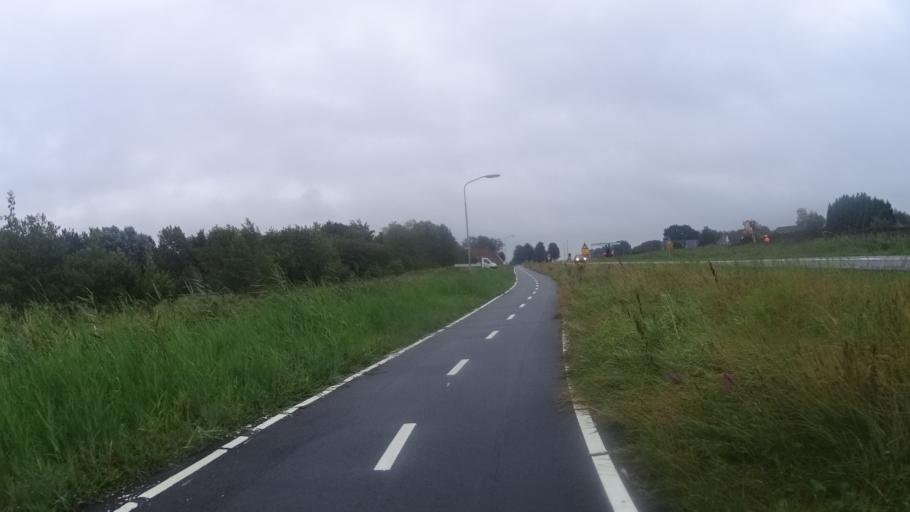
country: NL
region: Groningen
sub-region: Gemeente  Oldambt
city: Winschoten
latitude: 53.1626
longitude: 7.0188
